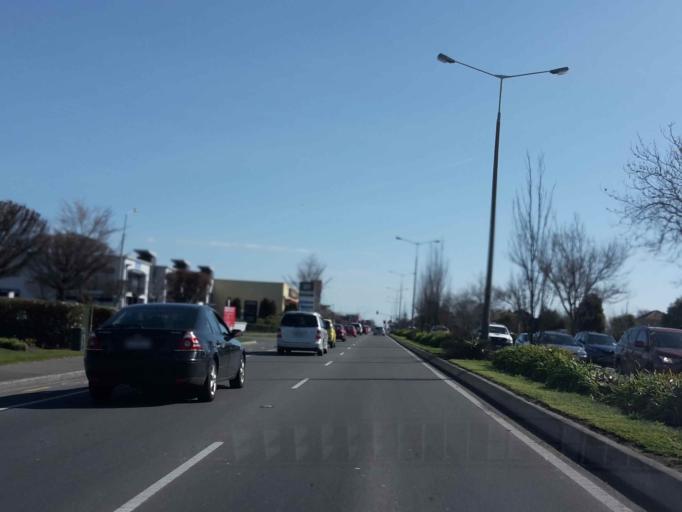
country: NZ
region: Canterbury
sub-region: Christchurch City
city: Christchurch
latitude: -43.5380
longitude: 172.5913
